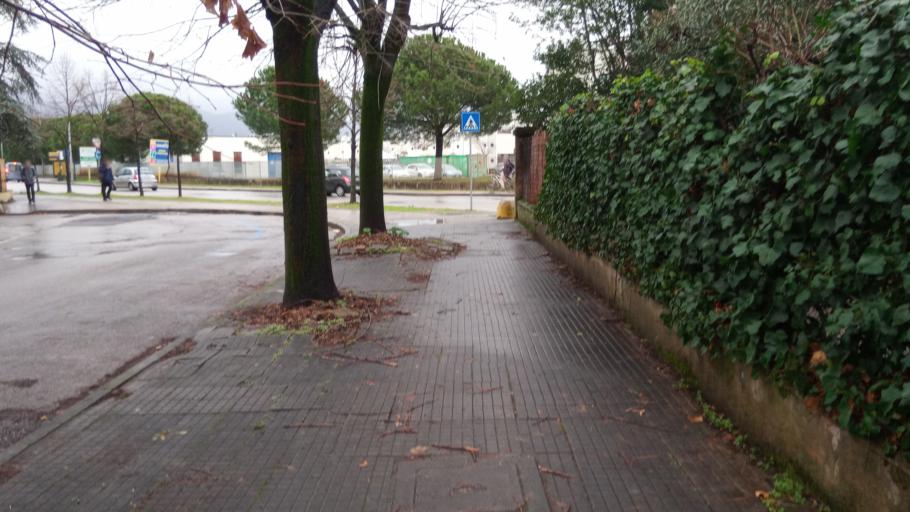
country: IT
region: Tuscany
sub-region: Province of Pisa
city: Pisa
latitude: 43.7195
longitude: 10.4199
